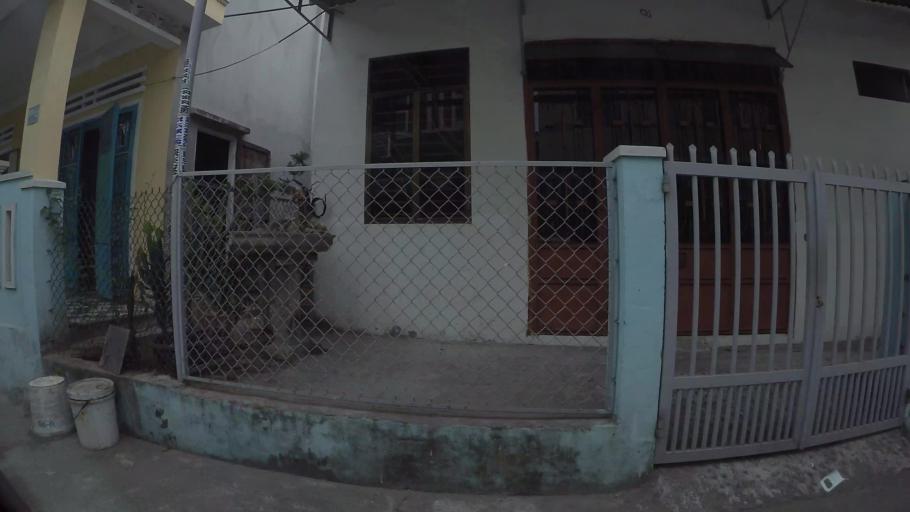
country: VN
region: Da Nang
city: Thanh Khe
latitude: 16.0714
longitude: 108.1831
